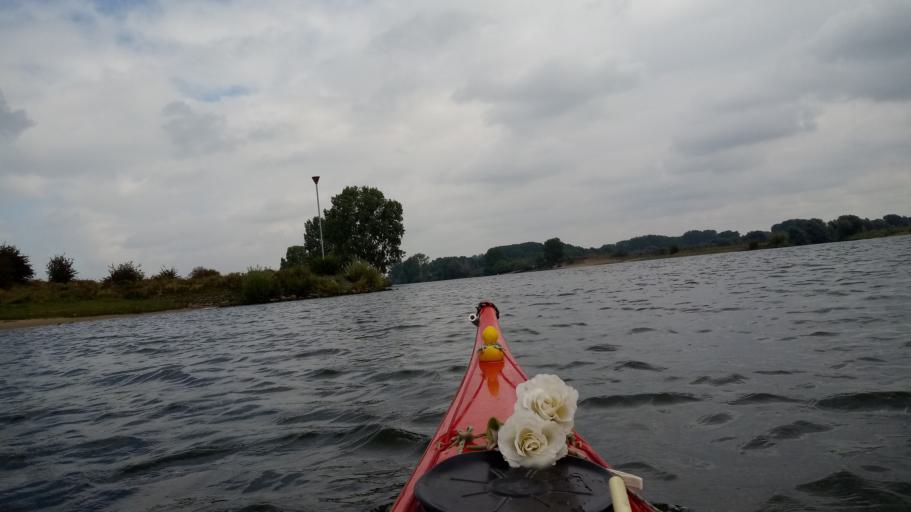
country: NL
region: Gelderland
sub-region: Gemeente Maasdriel
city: Hedel
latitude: 51.7346
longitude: 5.2519
